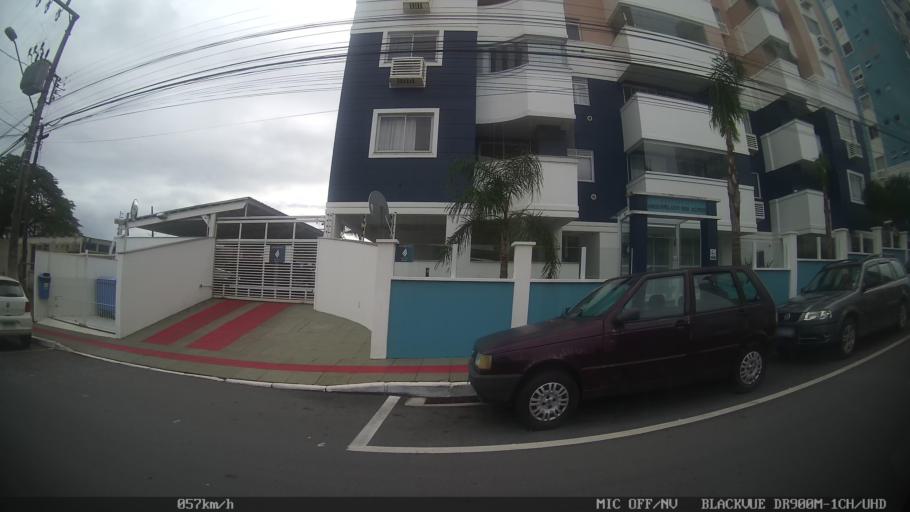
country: BR
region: Santa Catarina
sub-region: Sao Jose
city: Campinas
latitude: -27.5715
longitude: -48.6249
